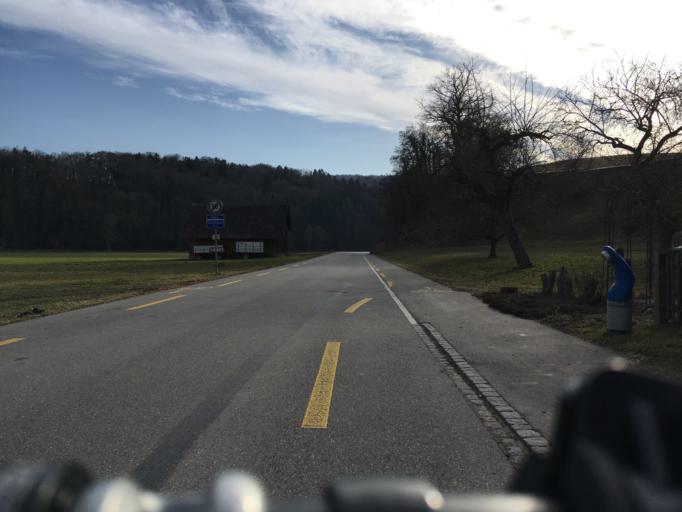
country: DE
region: Baden-Wuerttemberg
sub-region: Freiburg Region
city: Tengen
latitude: 47.7817
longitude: 8.6764
